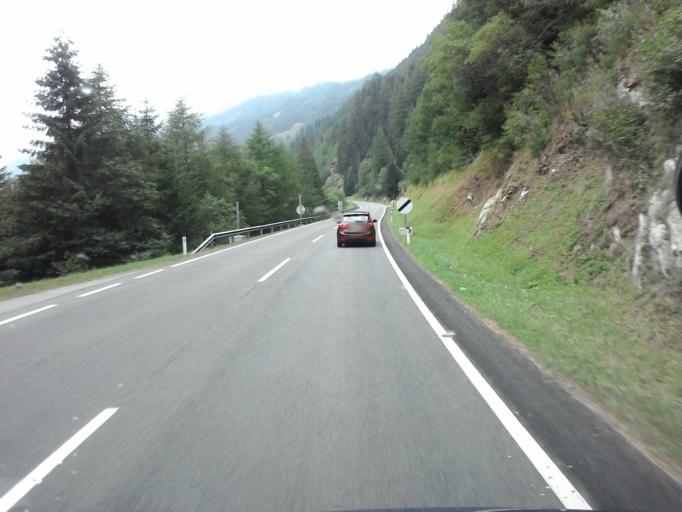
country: AT
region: Tyrol
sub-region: Politischer Bezirk Lienz
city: Matrei in Osttirol
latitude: 47.0786
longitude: 12.5309
